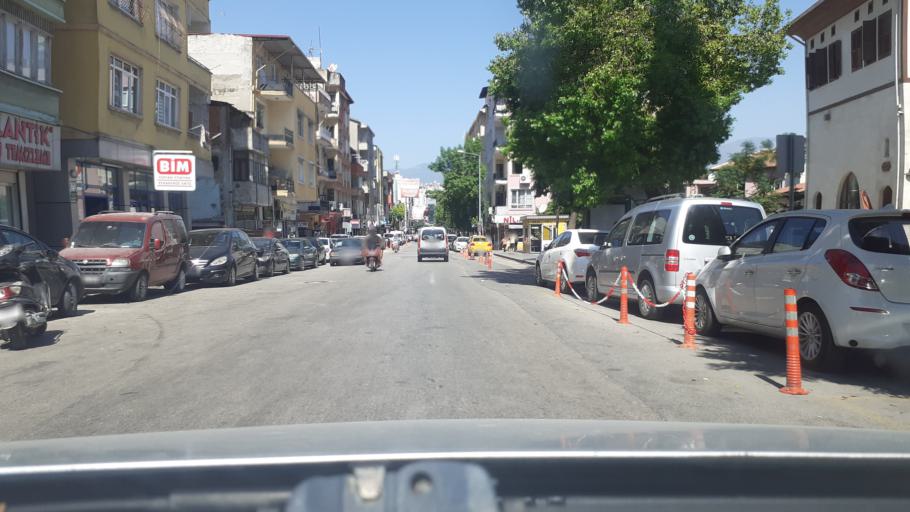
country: TR
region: Hatay
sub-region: Antakya Ilcesi
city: Antakya
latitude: 36.2014
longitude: 36.1651
